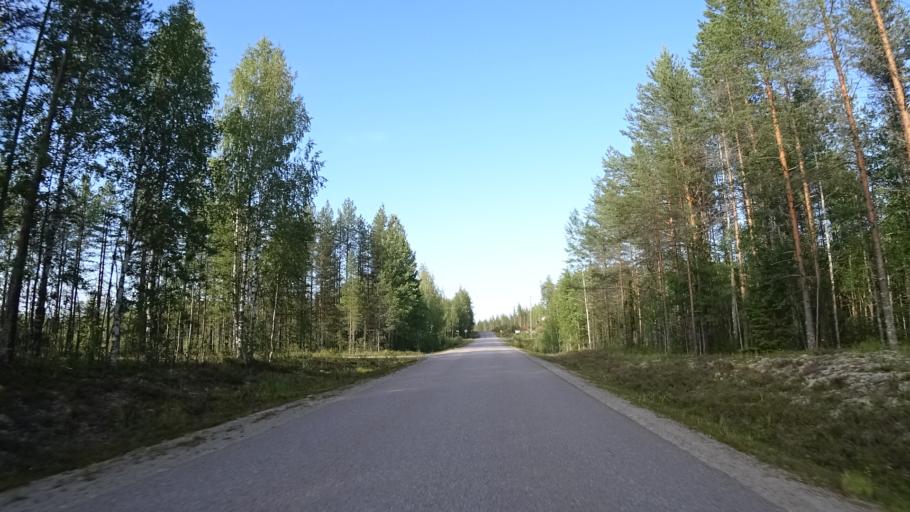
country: FI
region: North Karelia
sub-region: Joensuu
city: Eno
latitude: 63.0637
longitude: 30.5536
